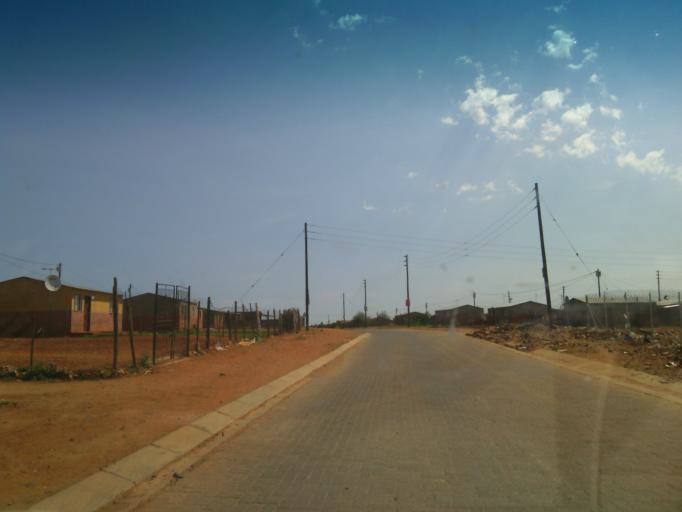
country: ZA
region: Northern Cape
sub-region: Frances Baard District Municipality
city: Barkly West
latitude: -28.5241
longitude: 24.5025
